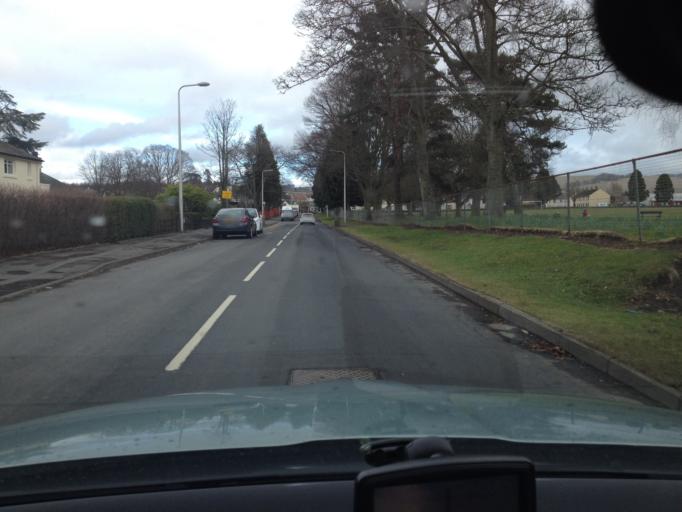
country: GB
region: Scotland
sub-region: Perth and Kinross
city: Scone
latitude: 56.4227
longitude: -3.4049
